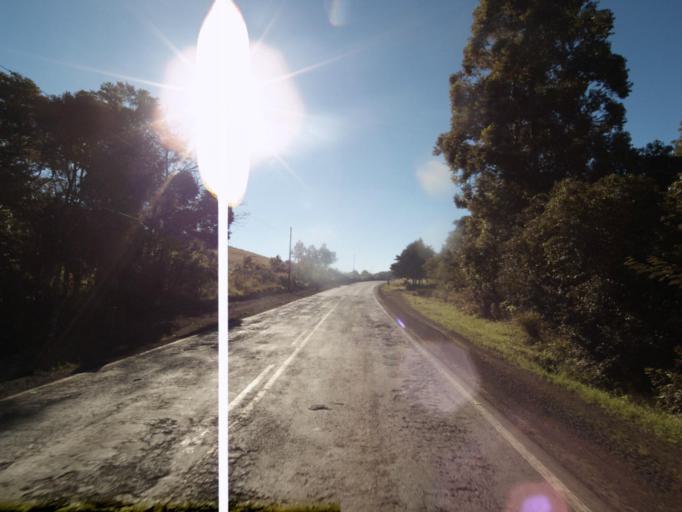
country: AR
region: Misiones
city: Bernardo de Irigoyen
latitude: -26.6191
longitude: -53.5185
